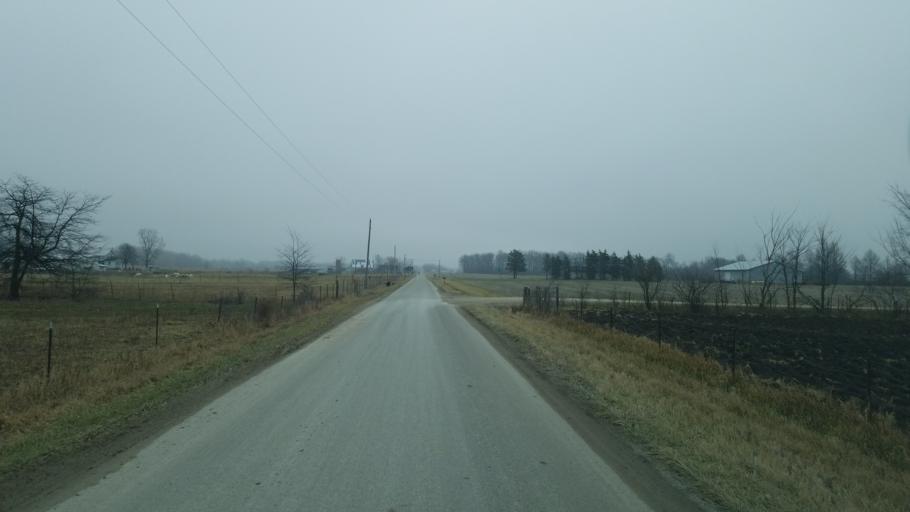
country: US
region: Indiana
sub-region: Adams County
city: Geneva
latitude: 40.5711
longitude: -84.8976
